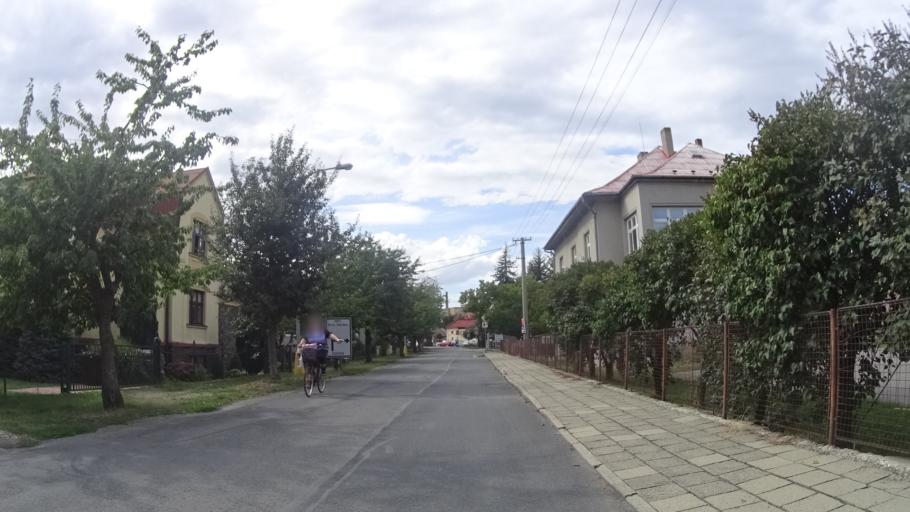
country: CZ
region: Olomoucky
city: Litovel
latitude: 49.7028
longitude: 17.0837
